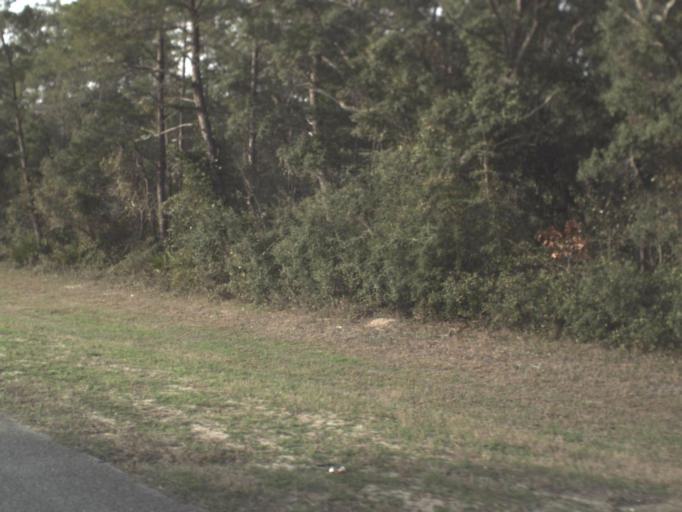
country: US
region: Florida
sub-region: Bay County
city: Mexico Beach
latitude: 29.9646
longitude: -85.4464
